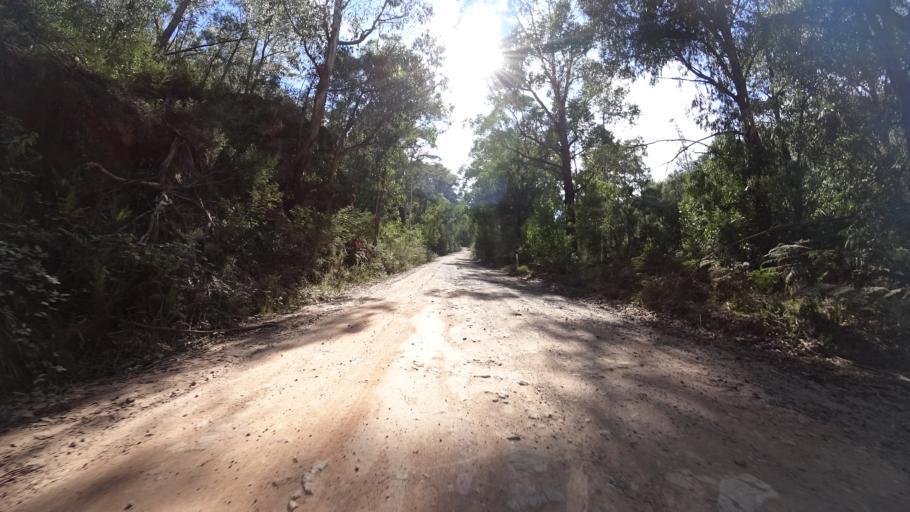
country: AU
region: New South Wales
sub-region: Lithgow
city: Lithgow
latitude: -33.4477
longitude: 150.1767
